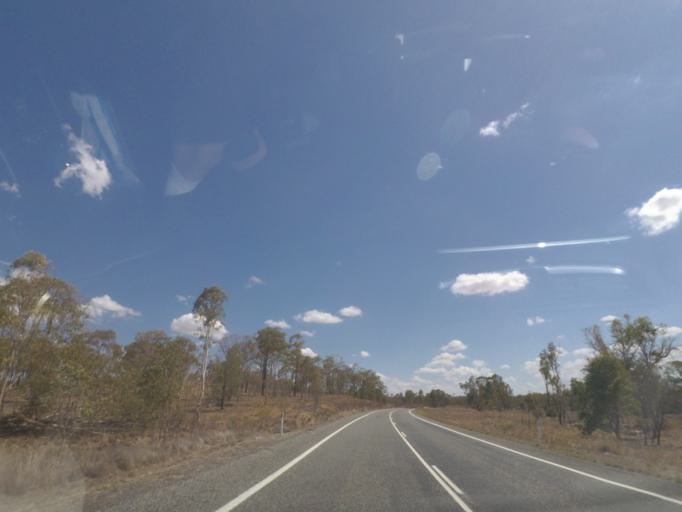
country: AU
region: Queensland
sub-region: Southern Downs
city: Warwick
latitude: -28.2131
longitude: 151.5640
